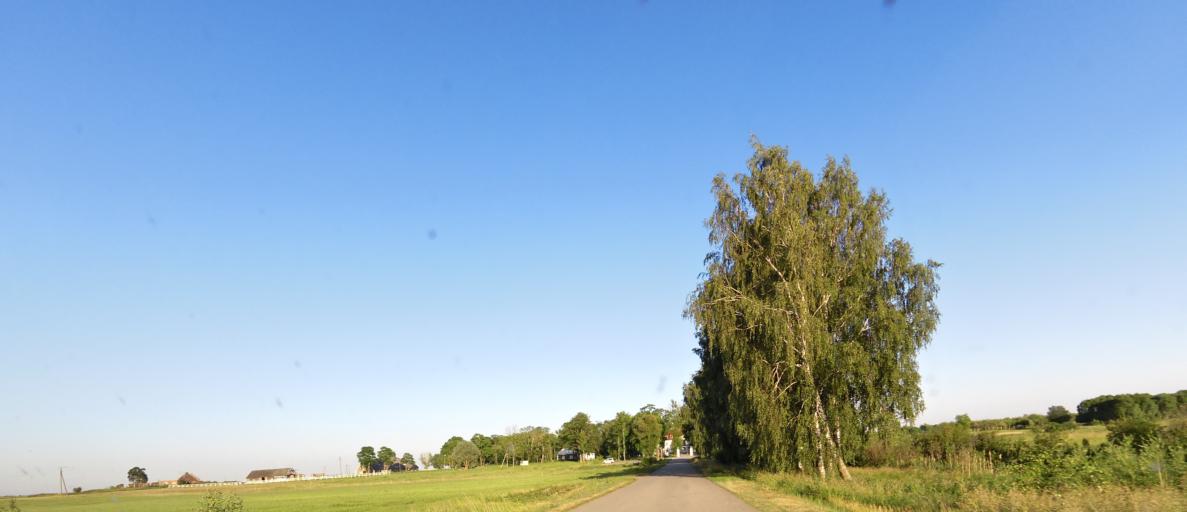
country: LT
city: Ramygala
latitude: 55.5990
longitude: 24.3520
